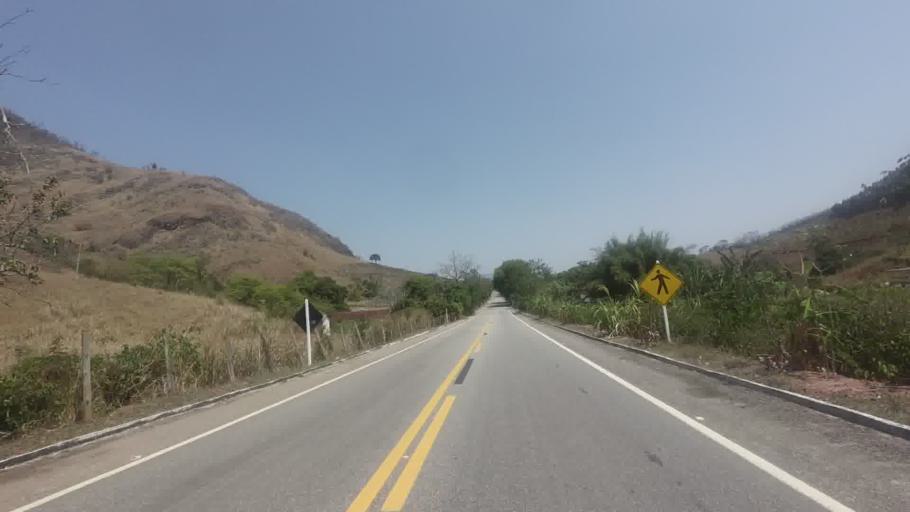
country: BR
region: Espirito Santo
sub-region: Cachoeiro De Itapemirim
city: Cachoeiro de Itapemirim
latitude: -20.8555
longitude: -41.2485
